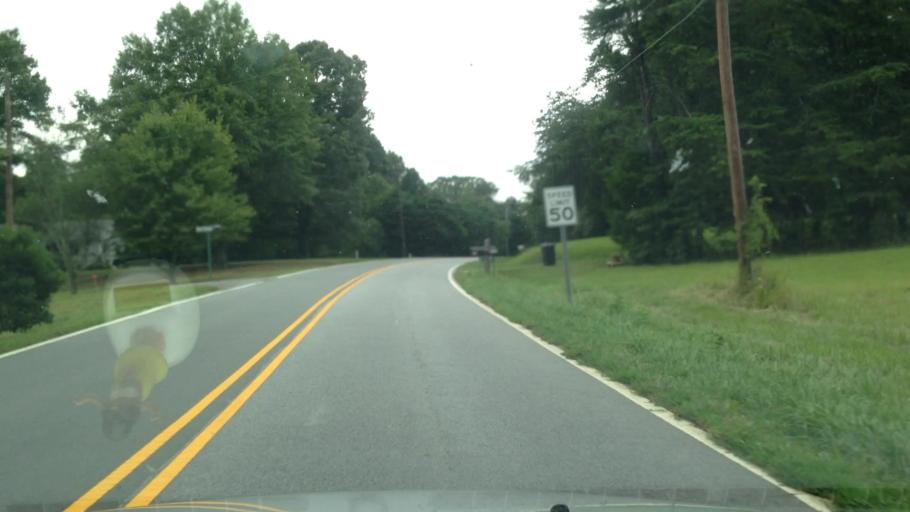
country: US
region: North Carolina
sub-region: Forsyth County
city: Walkertown
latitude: 36.1572
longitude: -80.1078
